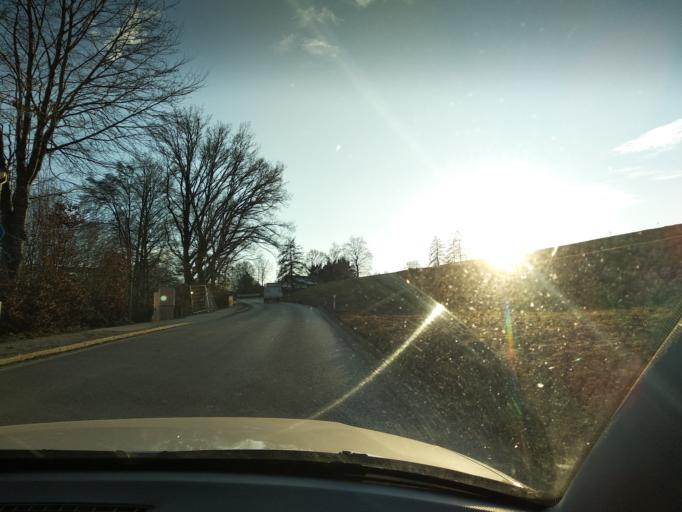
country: DE
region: Bavaria
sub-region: Upper Bavaria
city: Glonn
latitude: 47.9861
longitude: 11.8611
